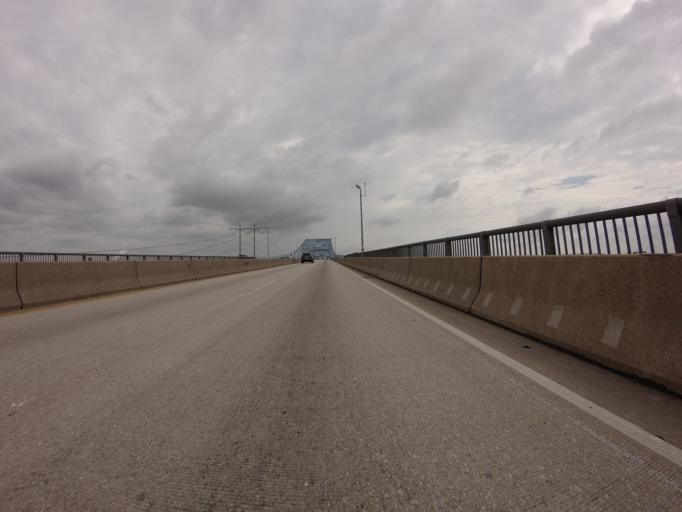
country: US
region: Pennsylvania
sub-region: Delaware County
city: Colwyn
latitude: 39.8966
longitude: -75.2141
